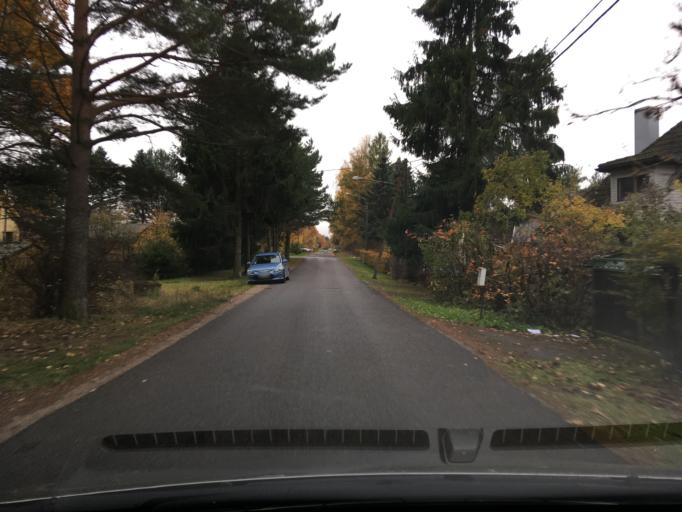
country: EE
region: Tartu
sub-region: Tartu linn
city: Tartu
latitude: 58.3513
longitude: 26.7788
